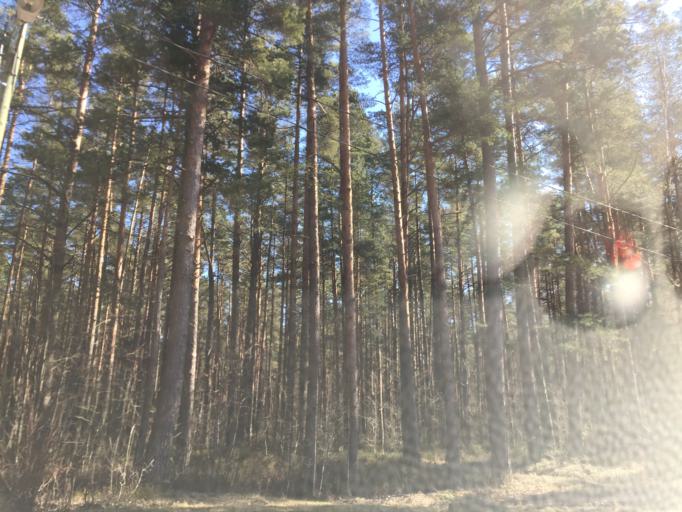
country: LV
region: Jurmala
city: Jurmala
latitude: 56.9494
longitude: 23.6845
